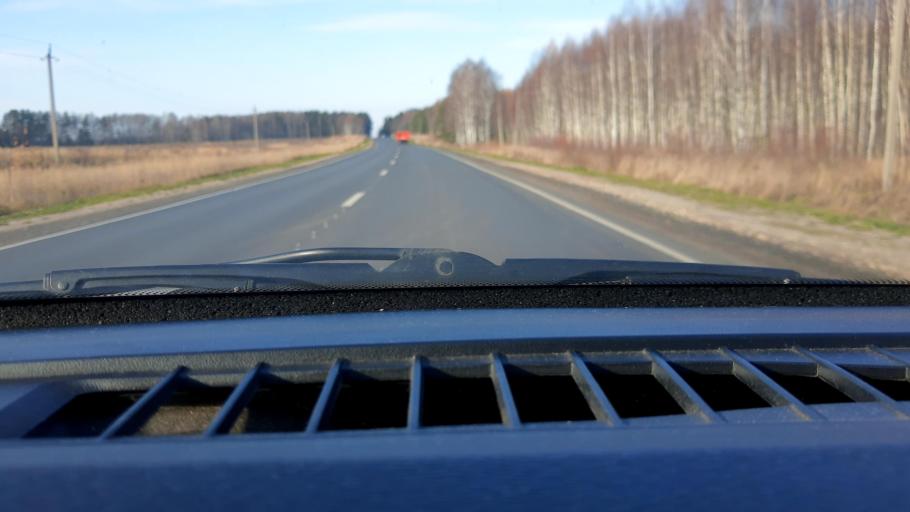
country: RU
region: Nizjnij Novgorod
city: Novaya Balakhna
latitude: 56.6117
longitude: 43.5999
